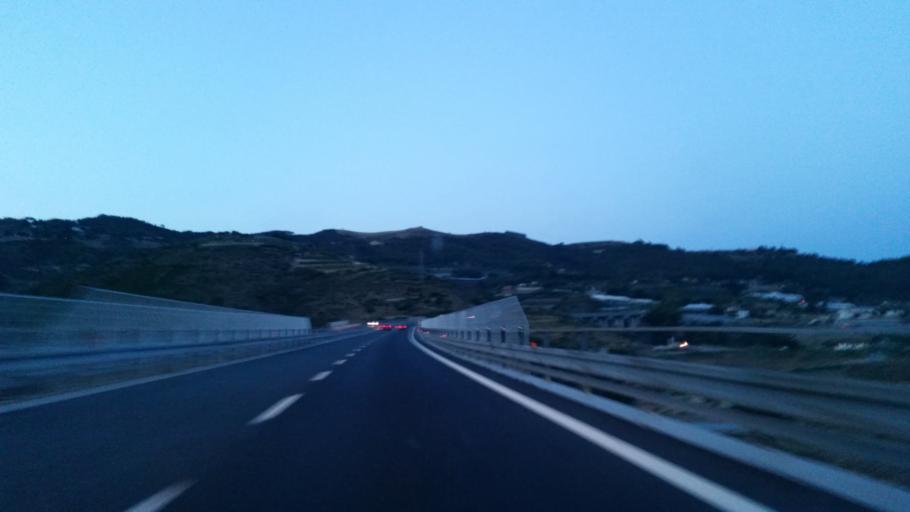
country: IT
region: Liguria
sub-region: Provincia di Imperia
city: Taggia
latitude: 43.8398
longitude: 7.8120
